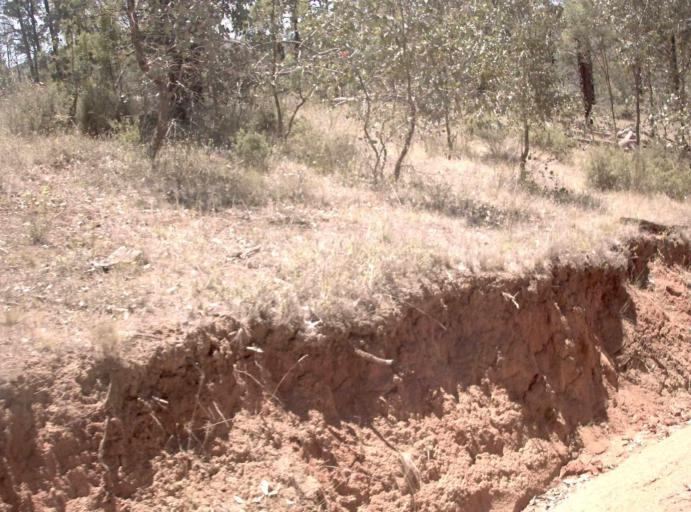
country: AU
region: New South Wales
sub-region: Snowy River
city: Jindabyne
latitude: -36.9267
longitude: 148.3881
